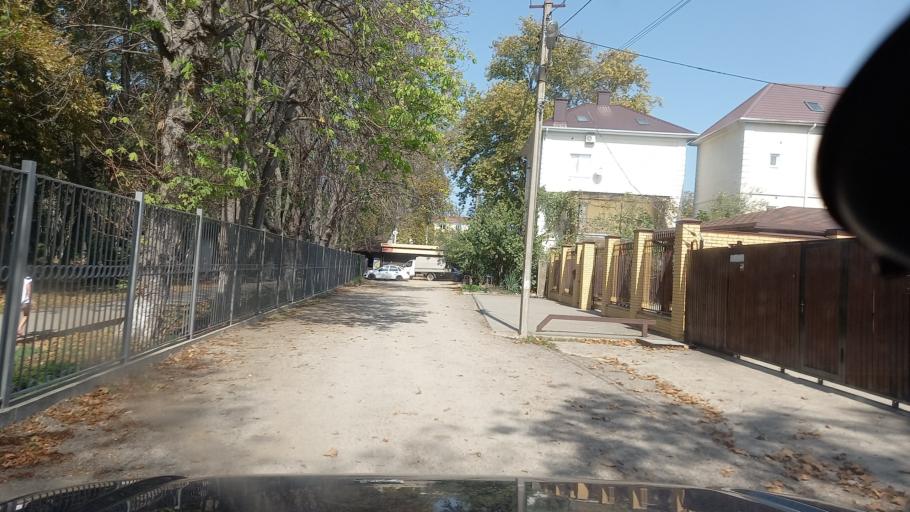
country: RU
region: Krasnodarskiy
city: Arkhipo-Osipovka
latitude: 44.3645
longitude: 38.5234
